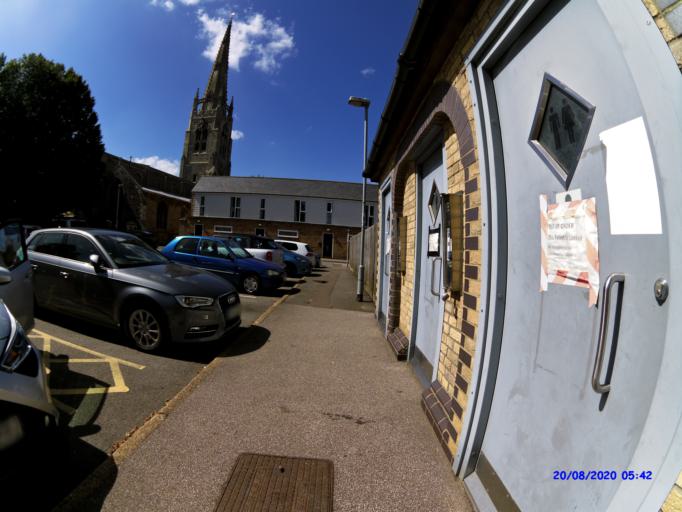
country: GB
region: England
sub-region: Cambridgeshire
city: Whittlesey
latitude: 52.5559
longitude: -0.1272
